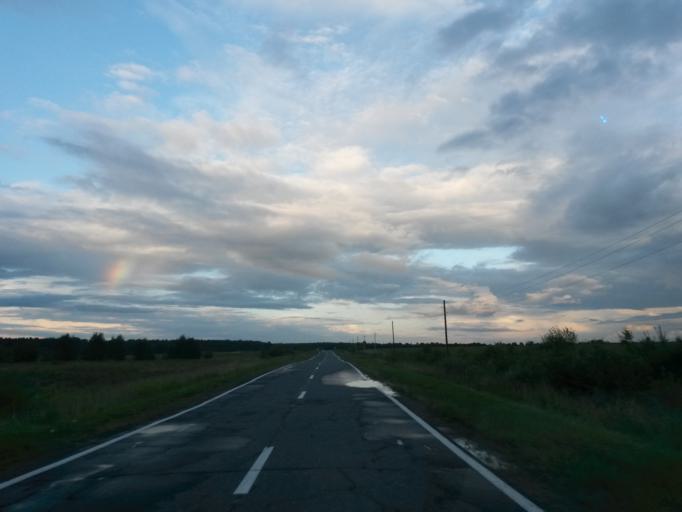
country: RU
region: Jaroslavl
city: Tutayev
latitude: 57.9485
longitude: 39.4686
